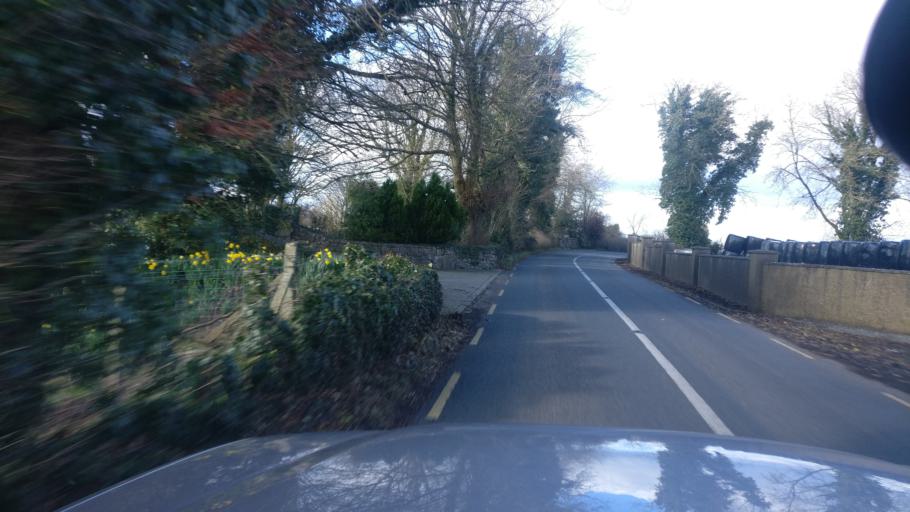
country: IE
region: Connaught
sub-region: County Galway
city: Loughrea
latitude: 53.1795
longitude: -8.3955
